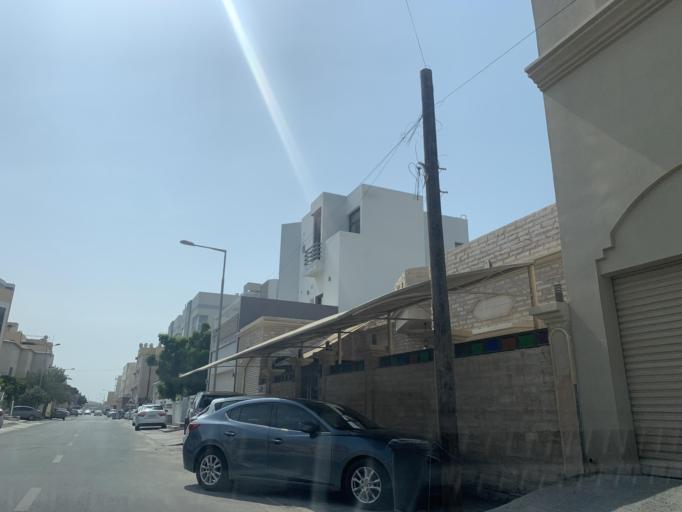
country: BH
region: Muharraq
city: Al Hadd
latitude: 26.2648
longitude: 50.6577
